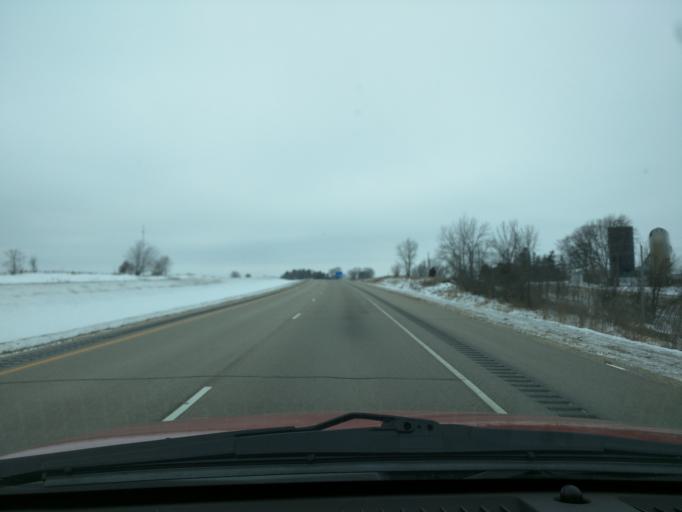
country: US
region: Minnesota
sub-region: Winona County
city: Winona
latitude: 43.9145
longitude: -91.5771
